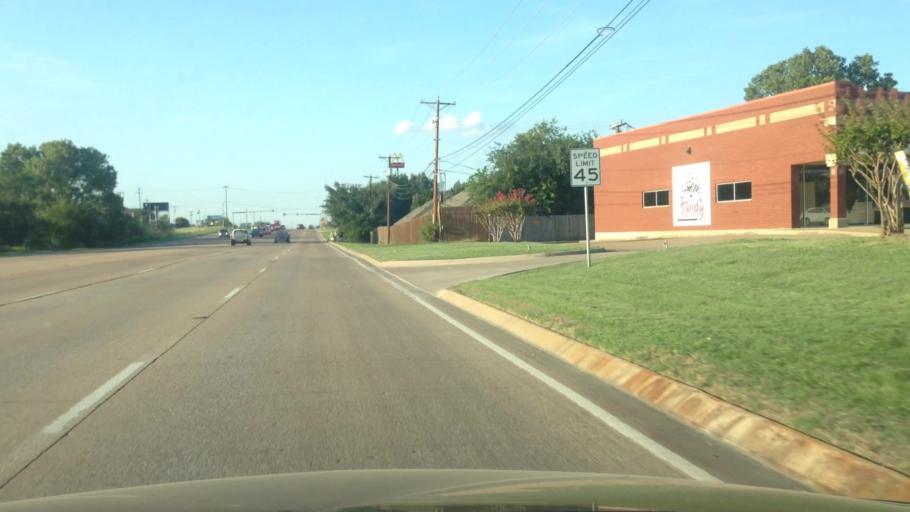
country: US
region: Texas
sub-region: Tarrant County
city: Watauga
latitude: 32.8709
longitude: -97.2624
